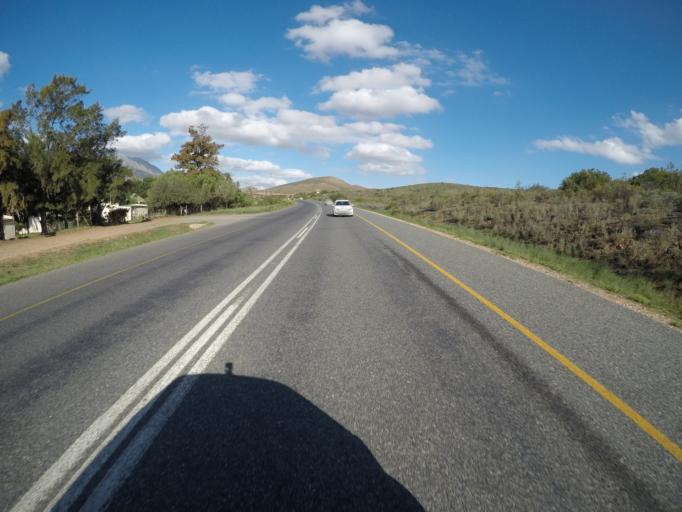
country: ZA
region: Western Cape
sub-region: Cape Winelands District Municipality
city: Ashton
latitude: -33.8637
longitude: 20.1170
